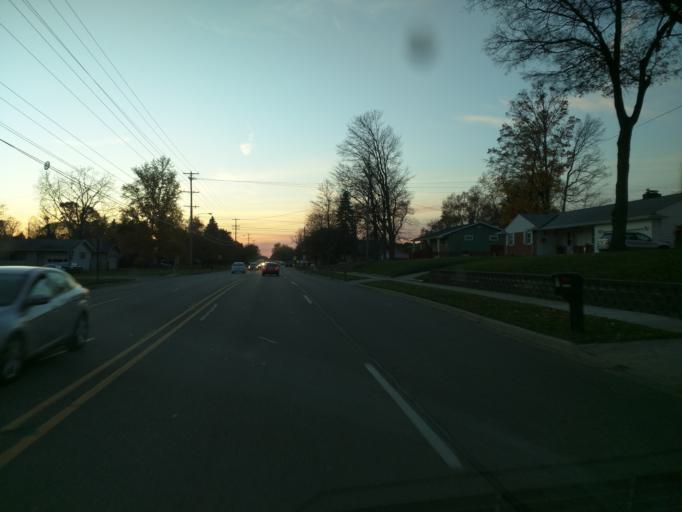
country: US
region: Michigan
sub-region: Eaton County
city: Waverly
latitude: 42.7338
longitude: -84.6078
